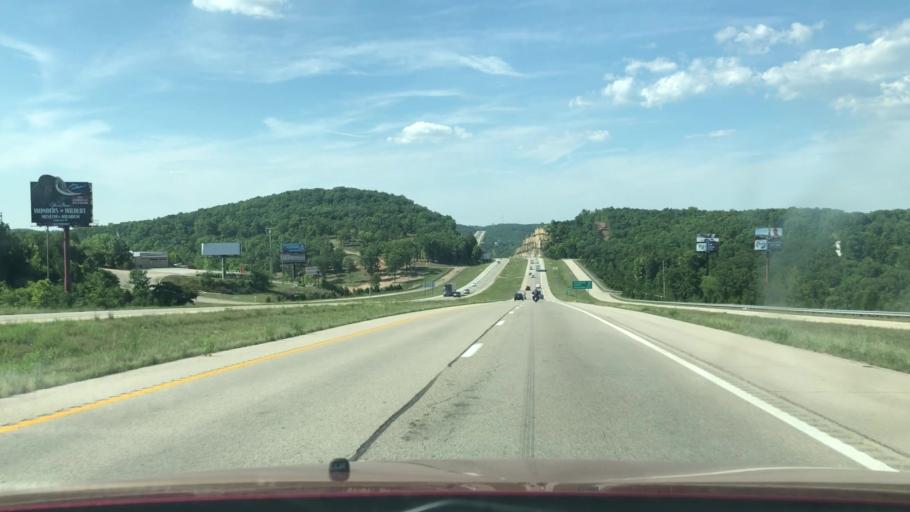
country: US
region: Missouri
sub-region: Taney County
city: Merriam Woods
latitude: 36.7542
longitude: -93.2226
